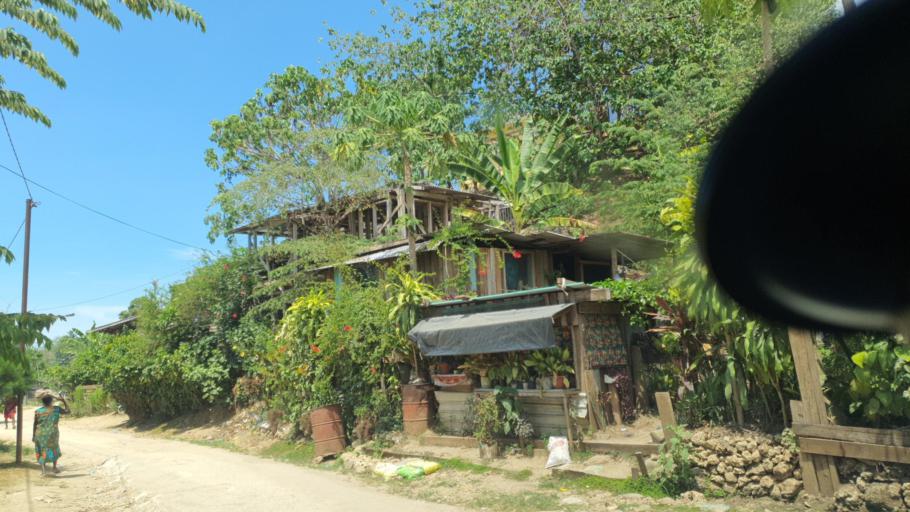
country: SB
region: Guadalcanal
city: Honiara
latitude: -9.4525
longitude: 159.9816
